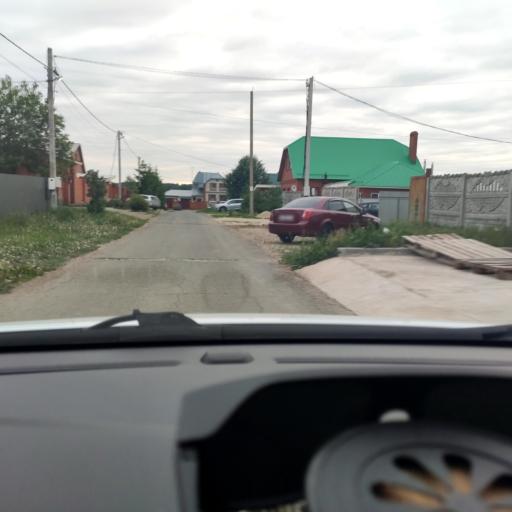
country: RU
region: Tatarstan
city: Vysokaya Gora
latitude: 55.9141
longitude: 49.3336
